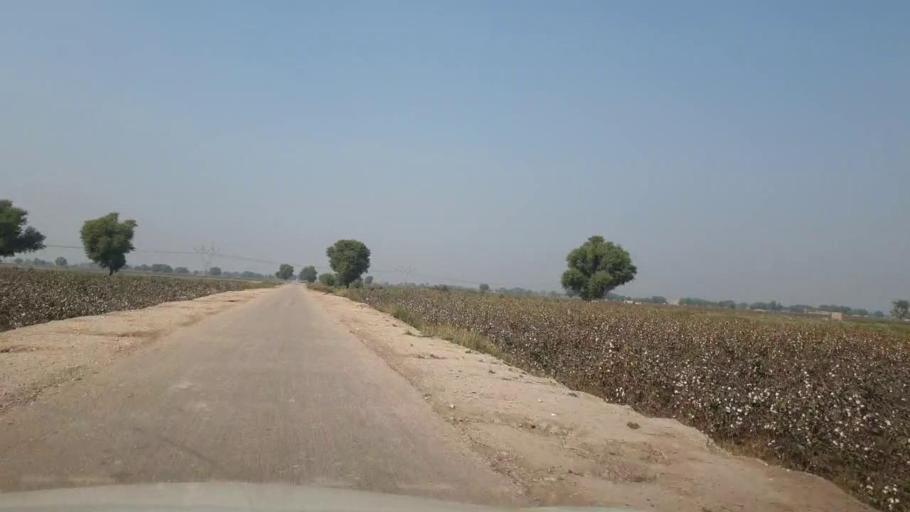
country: PK
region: Sindh
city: Bhan
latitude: 26.5306
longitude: 67.7536
